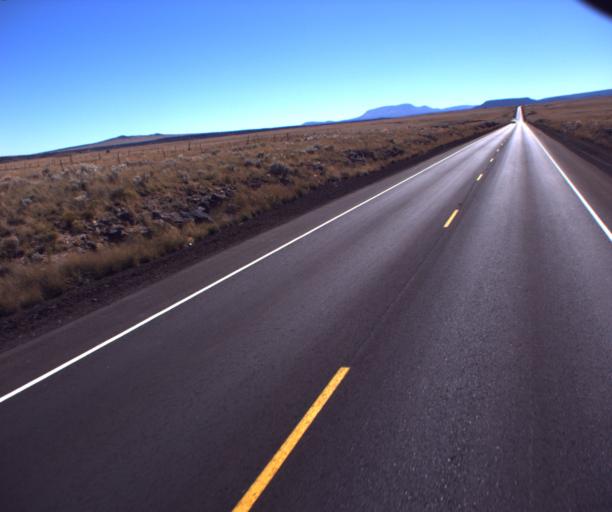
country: US
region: Arizona
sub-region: Apache County
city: Springerville
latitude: 34.2201
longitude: -109.3354
